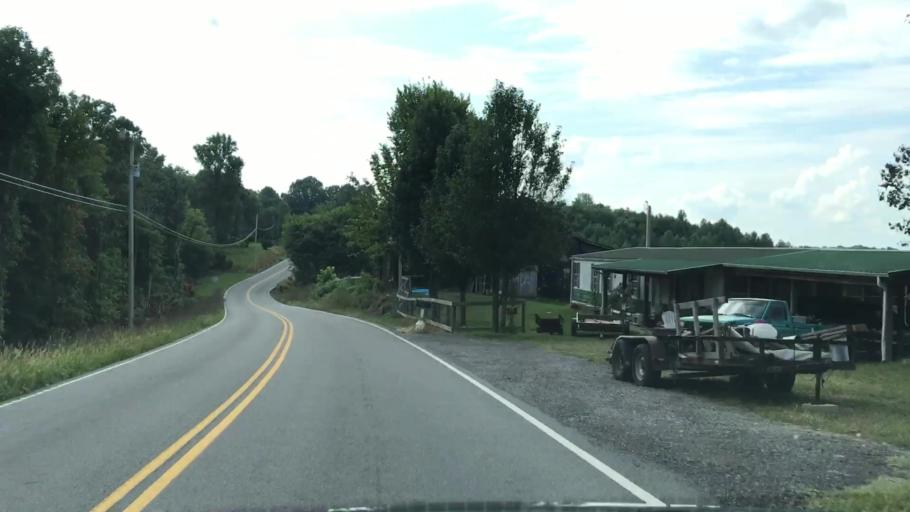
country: US
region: Tennessee
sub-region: Sumner County
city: Westmoreland
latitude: 36.5147
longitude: -86.1793
